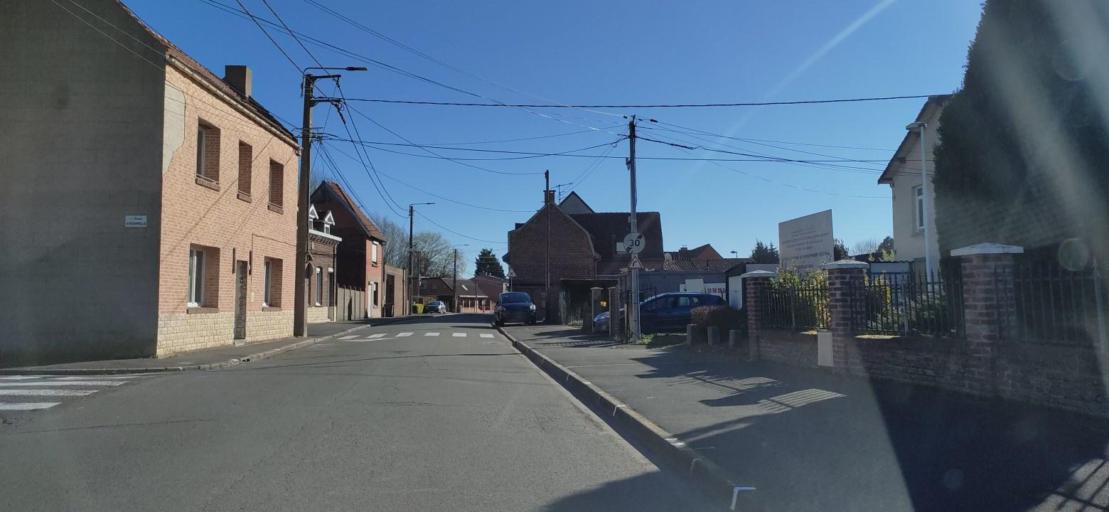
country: FR
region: Nord-Pas-de-Calais
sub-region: Departement du Nord
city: Camphin-en-Carembault
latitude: 50.4955
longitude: 2.9794
